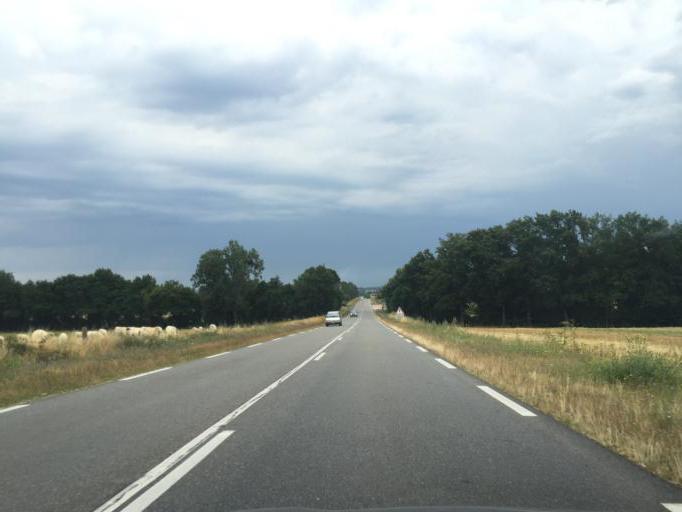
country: FR
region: Auvergne
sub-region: Departement de l'Allier
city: Lapalisse
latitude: 46.2478
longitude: 3.5980
